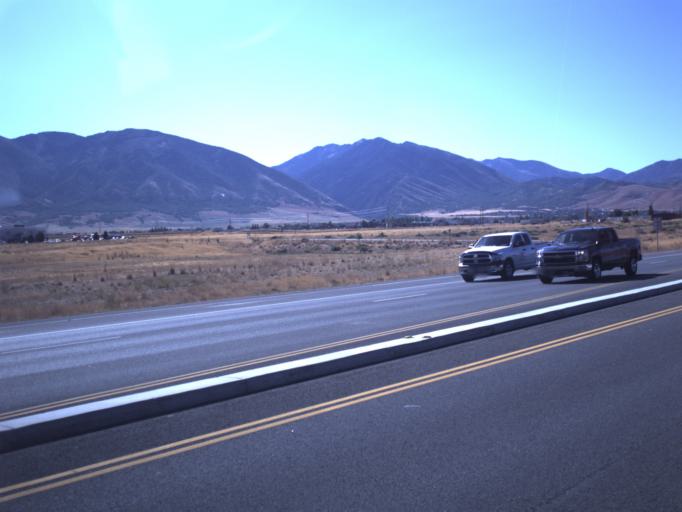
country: US
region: Utah
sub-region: Tooele County
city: Tooele
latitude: 40.5709
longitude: -112.2954
